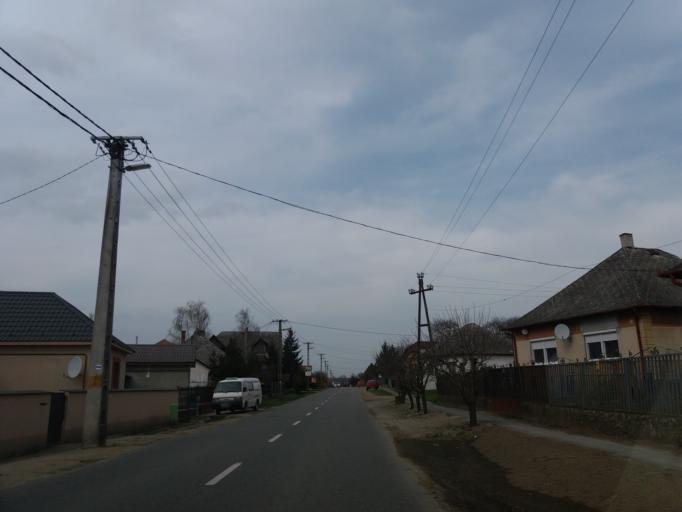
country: HU
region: Szabolcs-Szatmar-Bereg
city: Anarcs
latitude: 48.1772
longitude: 22.1002
